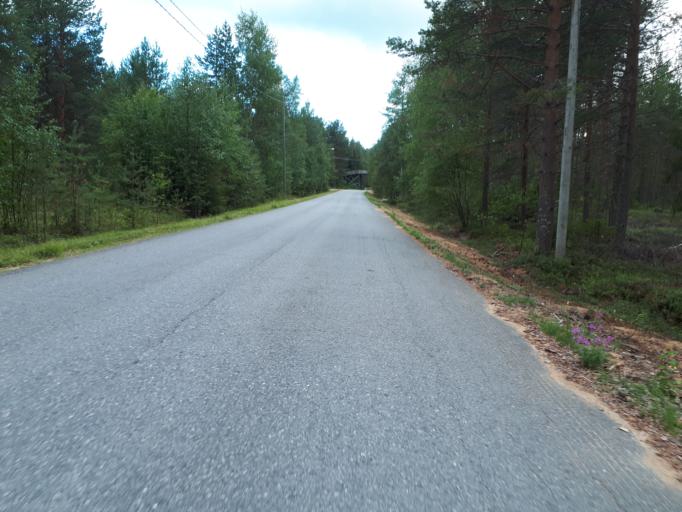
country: FI
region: Northern Ostrobothnia
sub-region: Oulunkaari
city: Ii
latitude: 65.3291
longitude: 25.3948
